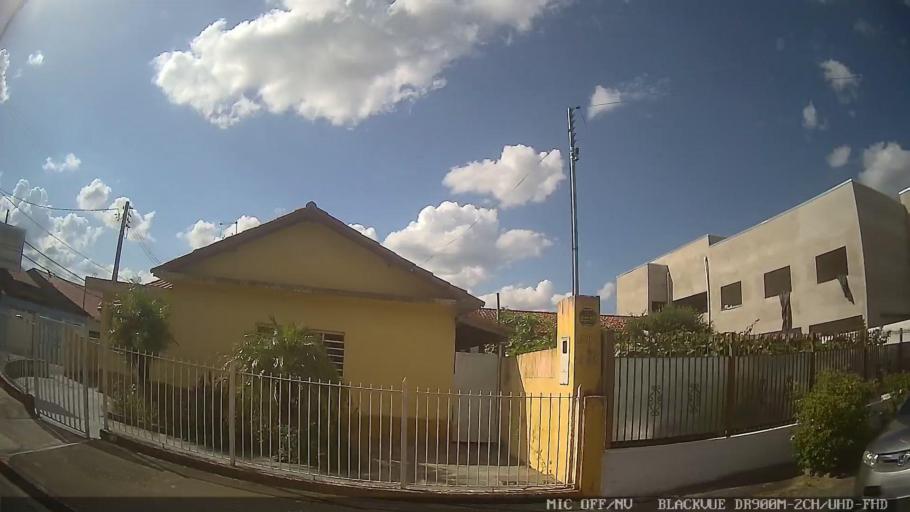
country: BR
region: Minas Gerais
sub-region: Extrema
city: Extrema
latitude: -22.8600
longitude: -46.3276
